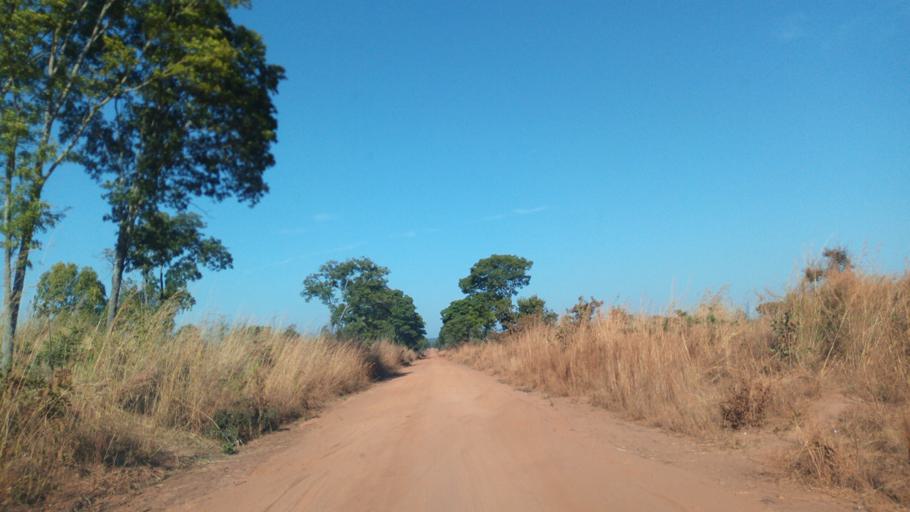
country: ZM
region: Luapula
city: Mwense
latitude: -10.5924
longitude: 28.4351
